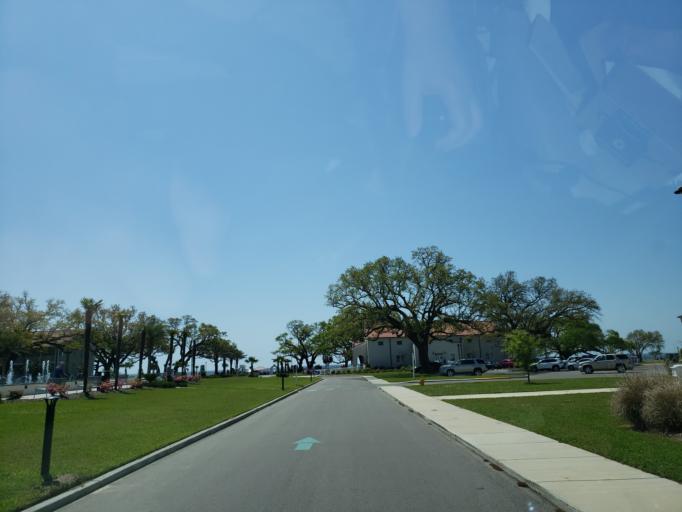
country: US
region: Mississippi
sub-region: Harrison County
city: Gulfport
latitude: 30.3783
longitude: -89.0526
